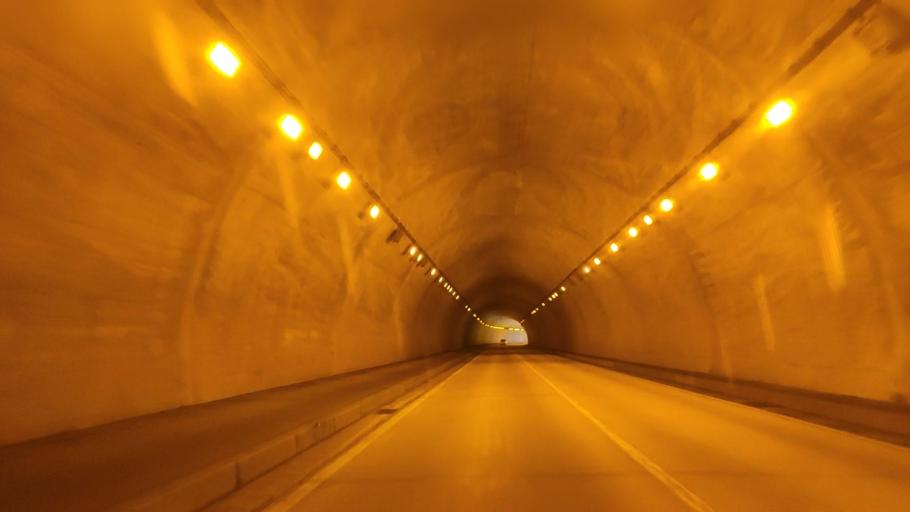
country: JP
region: Ishikawa
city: Nanao
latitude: 37.3839
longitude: 137.2334
